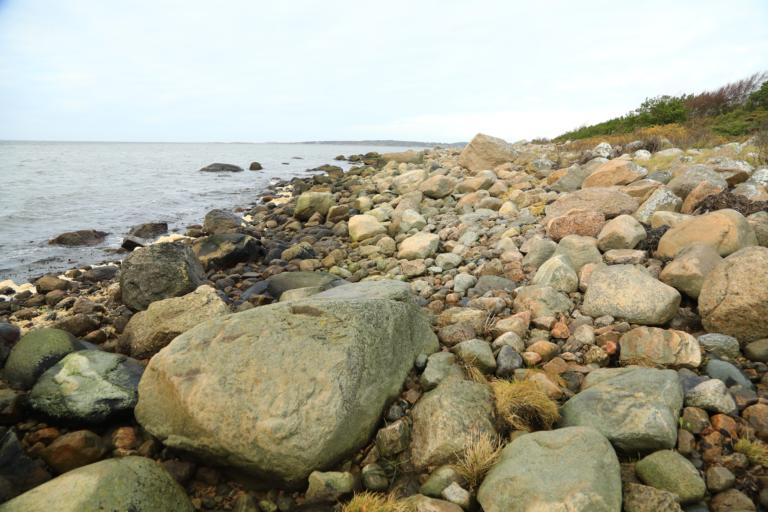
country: SE
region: Halland
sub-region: Varbergs Kommun
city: Varberg
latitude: 57.1713
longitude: 12.2039
